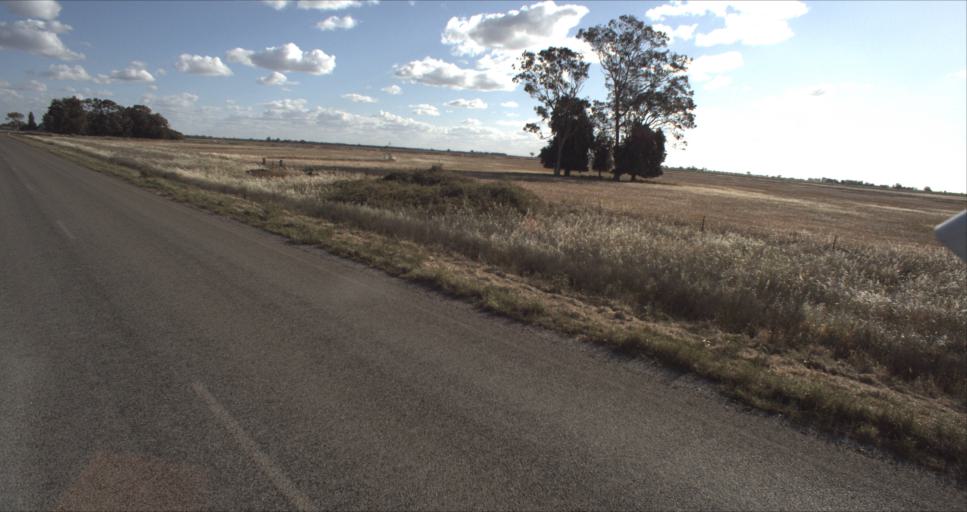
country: AU
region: New South Wales
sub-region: Leeton
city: Leeton
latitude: -34.5353
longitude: 146.2806
